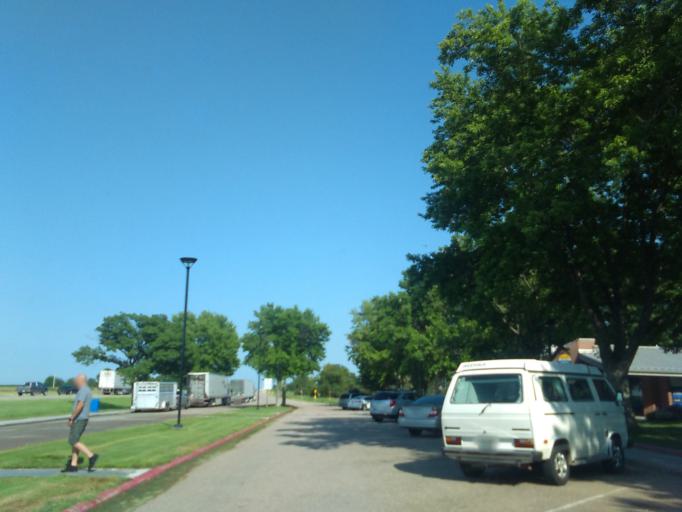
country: US
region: Nebraska
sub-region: Hall County
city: Grand Island
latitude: 40.8231
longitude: -98.3268
